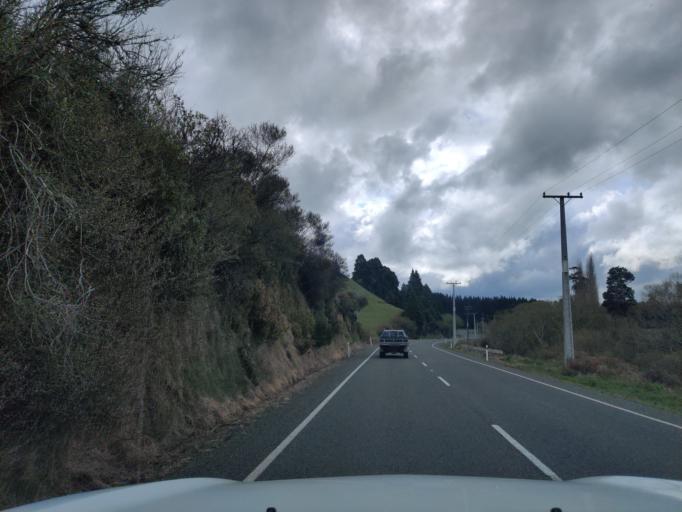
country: NZ
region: Manawatu-Wanganui
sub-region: Ruapehu District
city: Waiouru
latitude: -39.4438
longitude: 175.2877
